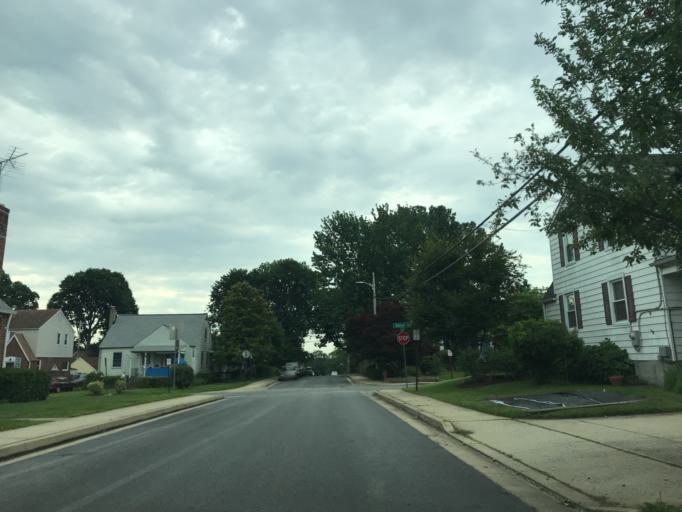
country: US
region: Maryland
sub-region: Baltimore County
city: Overlea
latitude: 39.3588
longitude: -76.5158
